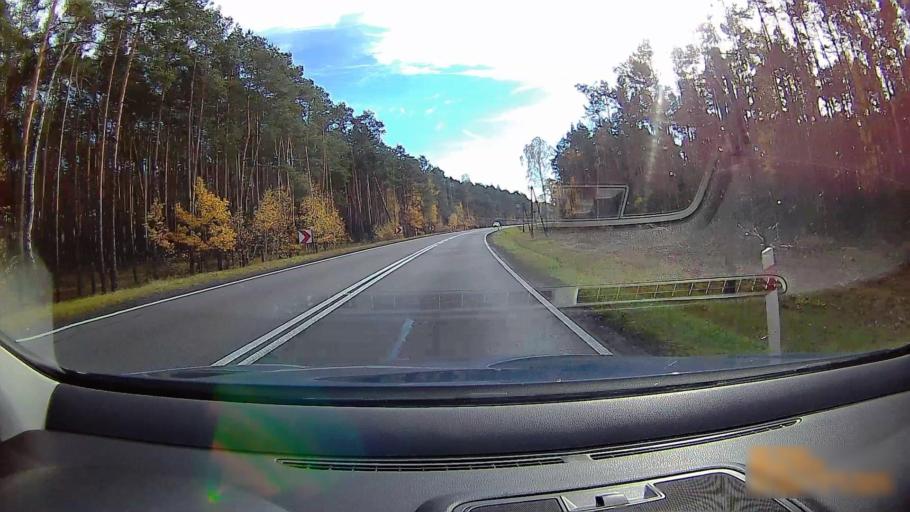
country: PL
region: Greater Poland Voivodeship
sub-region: Powiat ostrzeszowski
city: Ostrzeszow
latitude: 51.4800
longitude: 17.8852
